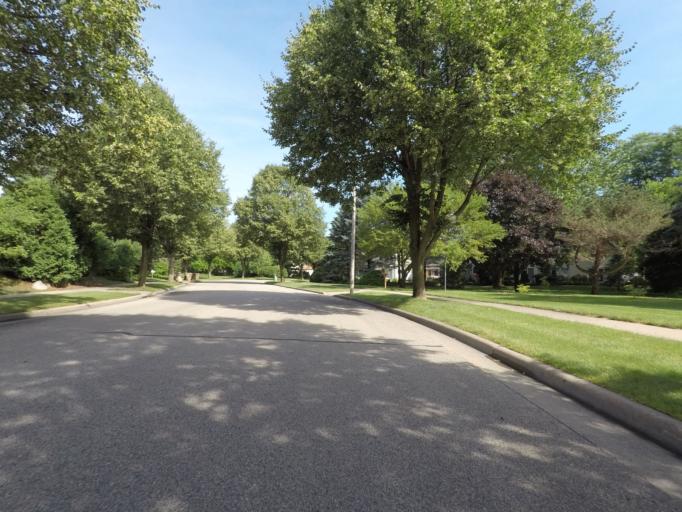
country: US
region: Wisconsin
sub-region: Dane County
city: Middleton
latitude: 43.0760
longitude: -89.4931
